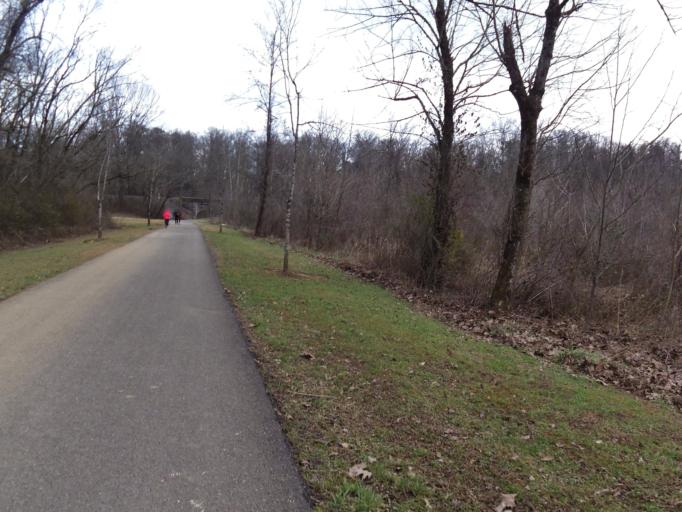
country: US
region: Tennessee
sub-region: Knox County
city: Knoxville
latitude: 35.9492
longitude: -83.9667
